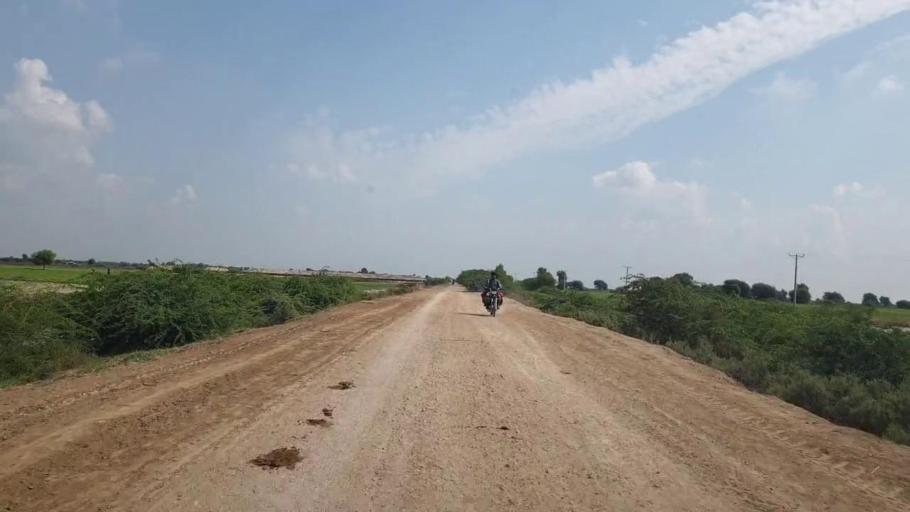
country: PK
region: Sindh
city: Badin
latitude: 24.4774
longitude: 68.6290
